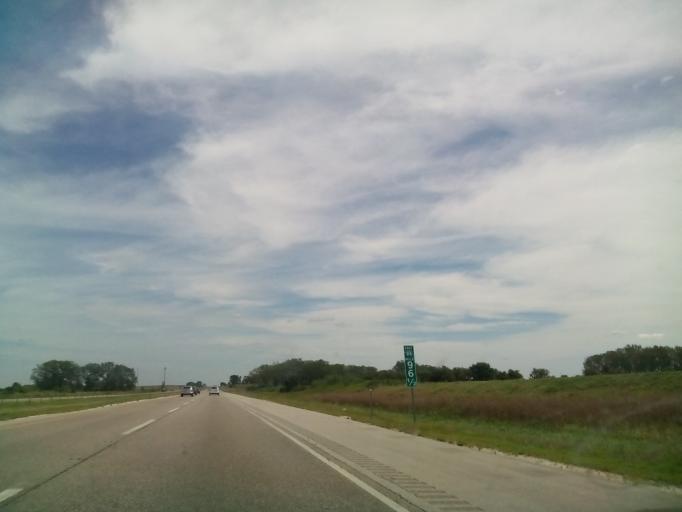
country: US
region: Illinois
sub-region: DeKalb County
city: Cortland
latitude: 41.9007
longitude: -88.6766
